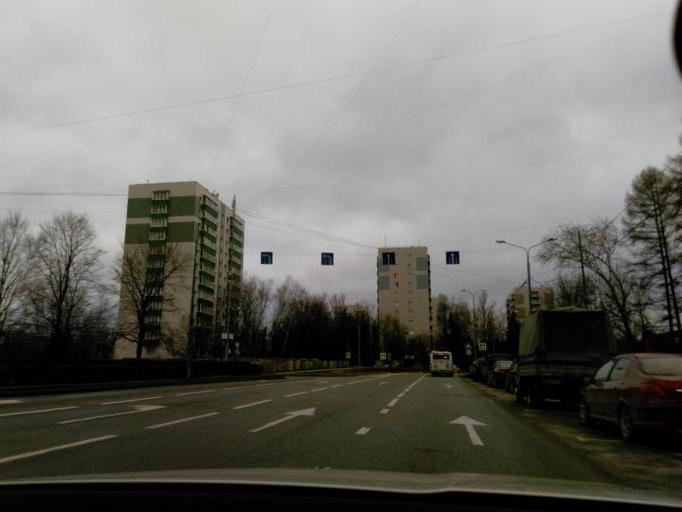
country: RU
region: Moskovskaya
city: Rzhavki
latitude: 55.9909
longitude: 37.2250
